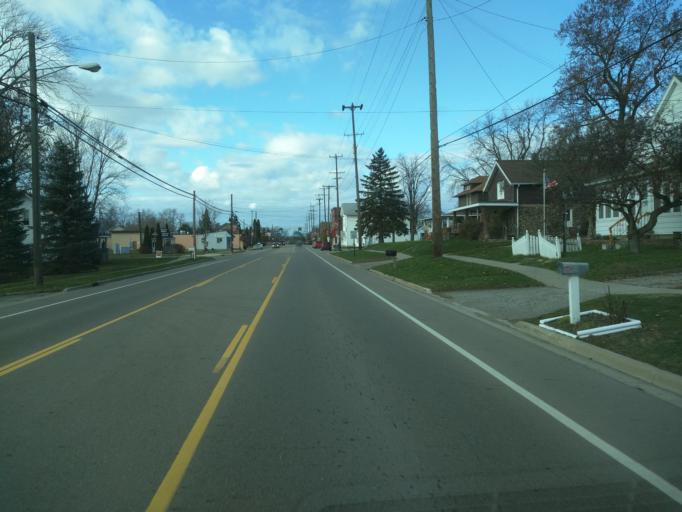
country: US
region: Michigan
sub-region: Ingham County
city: Webberville
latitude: 42.6670
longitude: -84.1719
